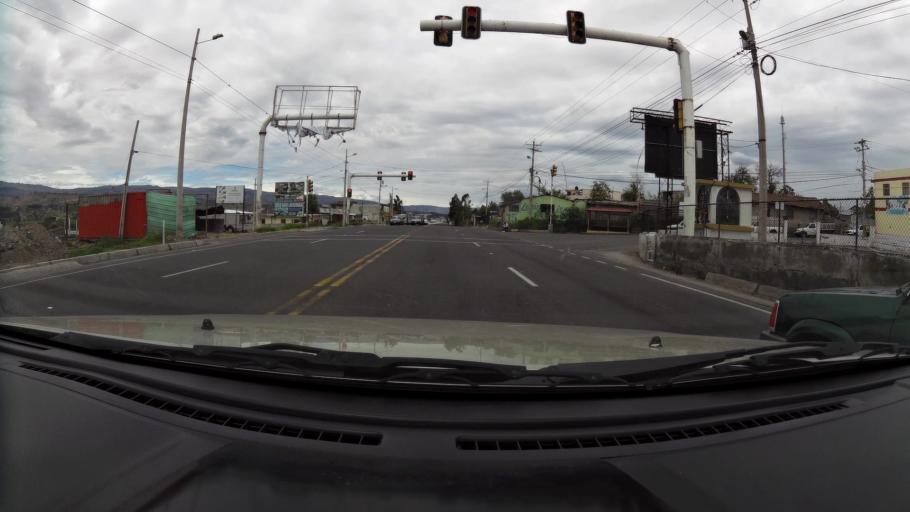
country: EC
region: Cotopaxi
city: Latacunga
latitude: -0.9791
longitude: -78.6058
